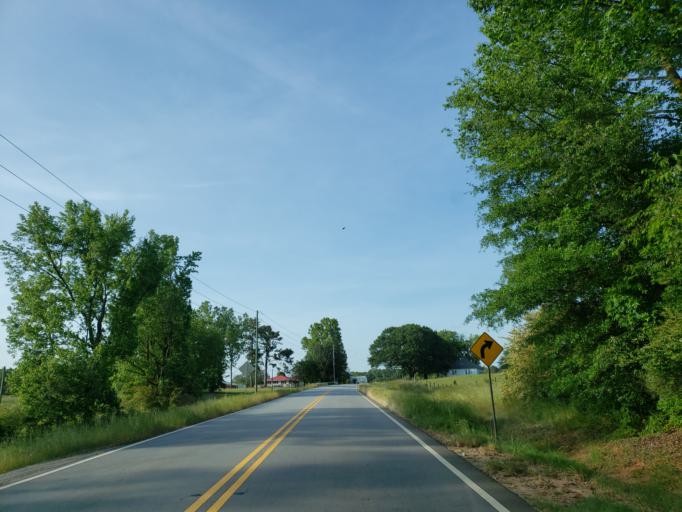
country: US
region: Georgia
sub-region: Carroll County
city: Bowdon
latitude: 33.4760
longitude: -85.2903
